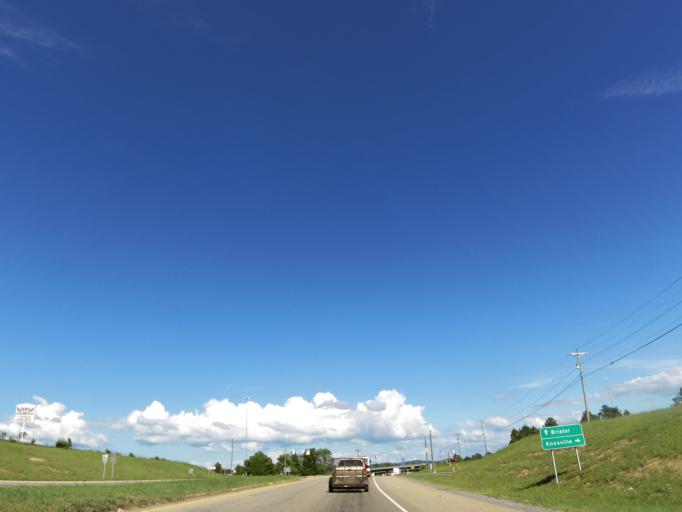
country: US
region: Tennessee
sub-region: Greene County
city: Mosheim
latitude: 36.2249
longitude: -83.0446
